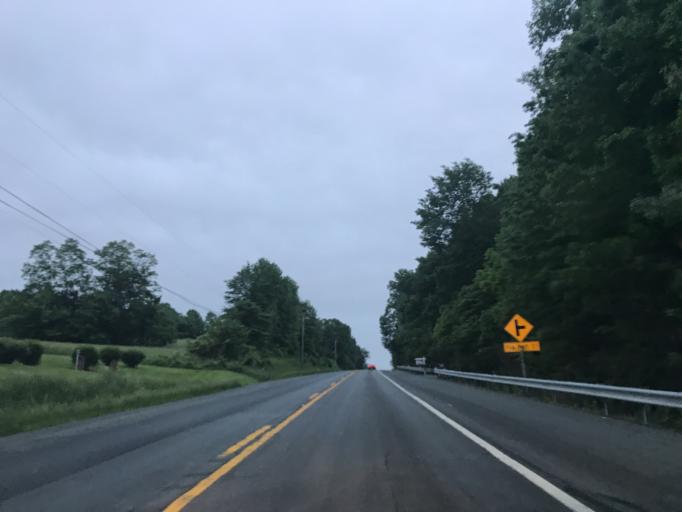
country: US
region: Maryland
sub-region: Frederick County
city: Linganore
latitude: 39.4153
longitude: -77.2541
